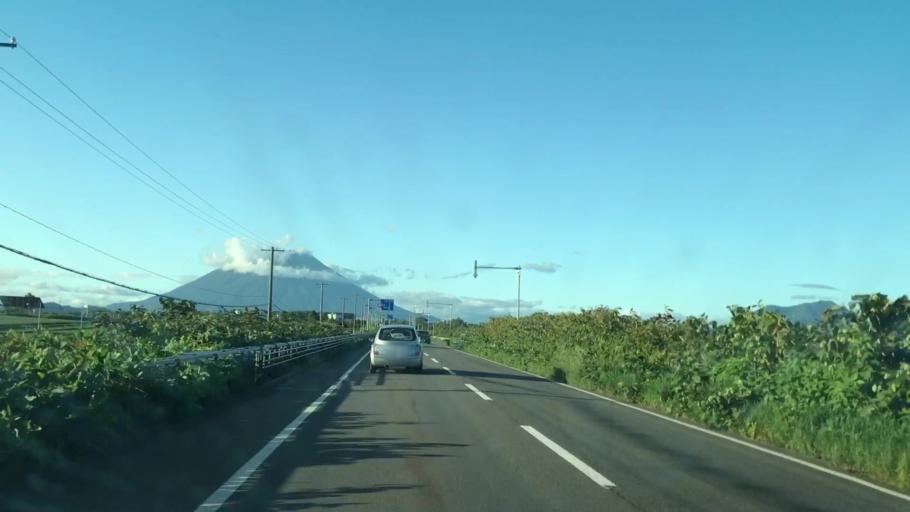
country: JP
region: Hokkaido
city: Niseko Town
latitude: 42.6577
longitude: 140.8114
